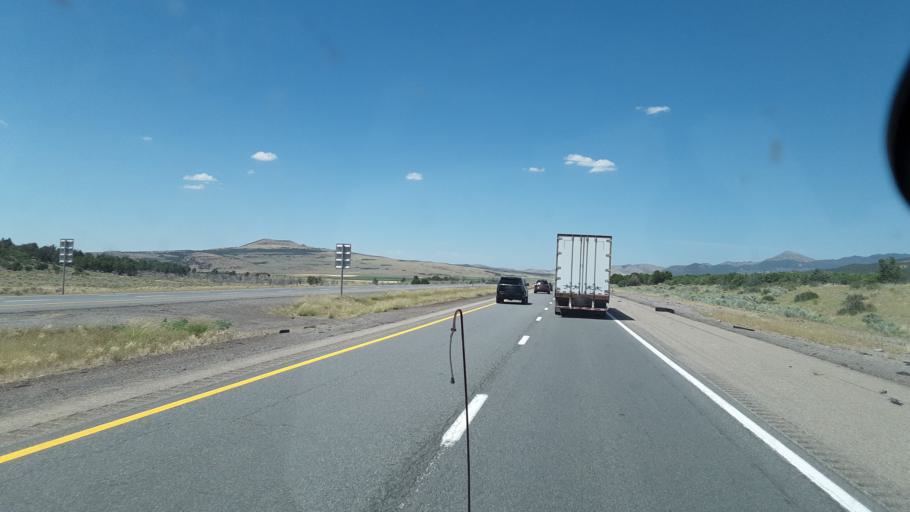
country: US
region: Utah
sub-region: Beaver County
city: Beaver
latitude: 38.4987
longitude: -112.6154
